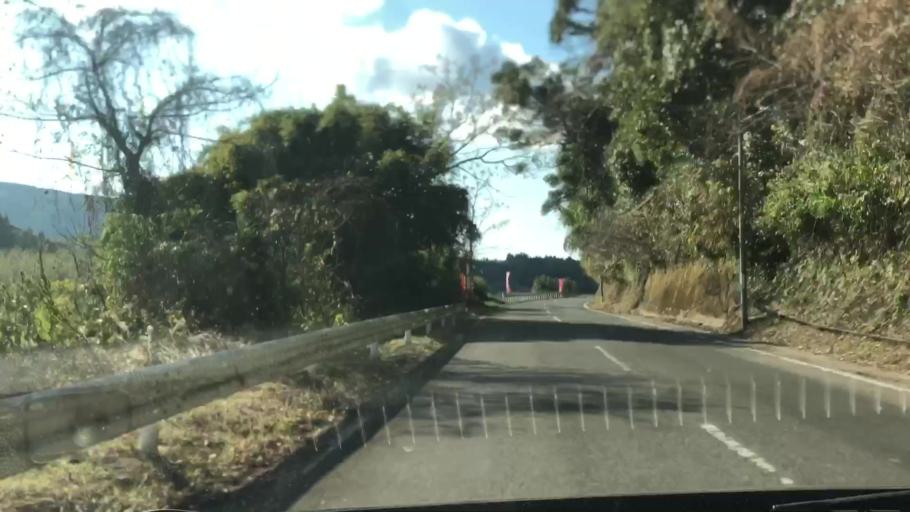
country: JP
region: Kagoshima
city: Satsumasendai
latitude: 31.8590
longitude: 130.3557
